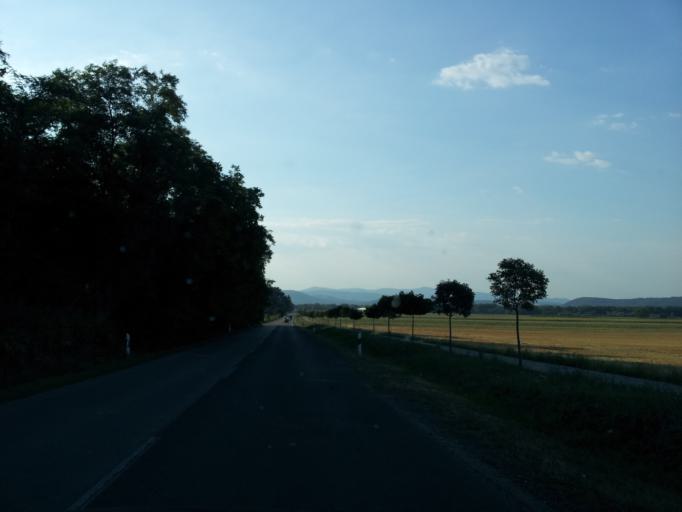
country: HU
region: Pest
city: Dunabogdany
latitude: 47.7743
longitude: 19.0569
